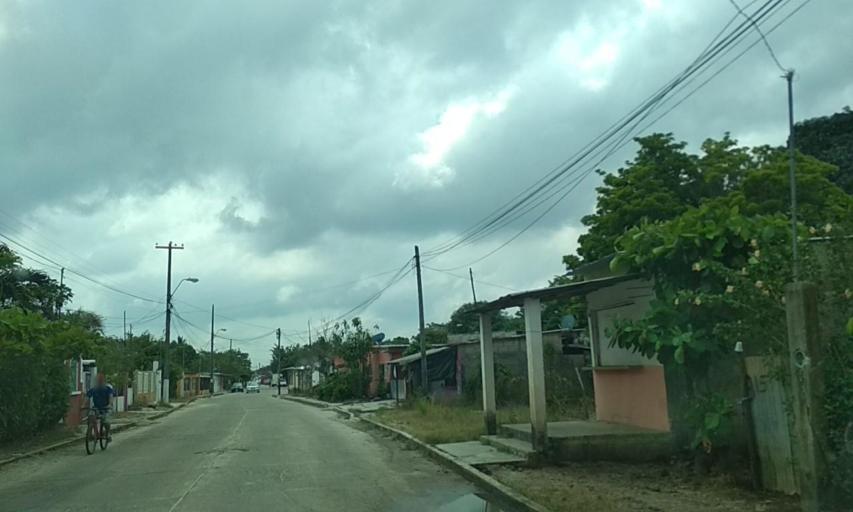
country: MX
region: Veracruz
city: Las Choapas
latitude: 17.9004
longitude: -94.1041
